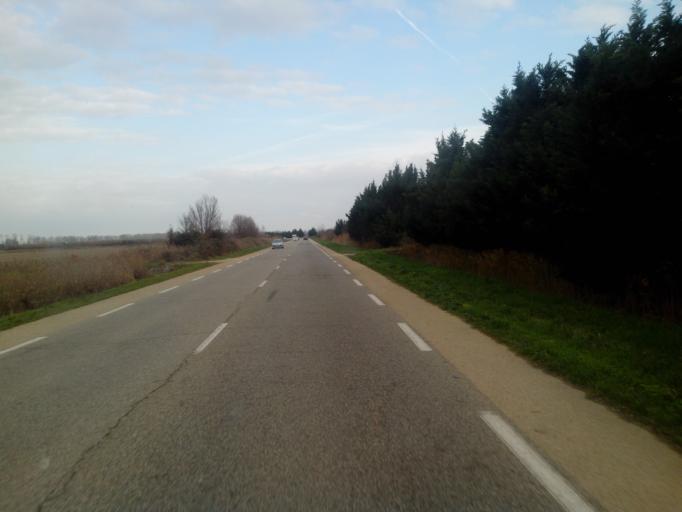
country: FR
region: Languedoc-Roussillon
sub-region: Departement du Gard
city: Saint-Gilles
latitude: 43.5754
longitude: 4.4268
